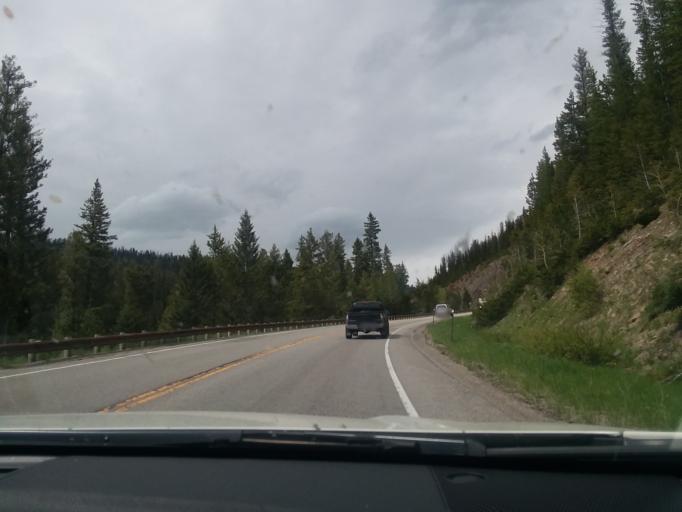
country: US
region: Wyoming
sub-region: Teton County
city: Wilson
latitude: 43.4990
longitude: -110.9252
